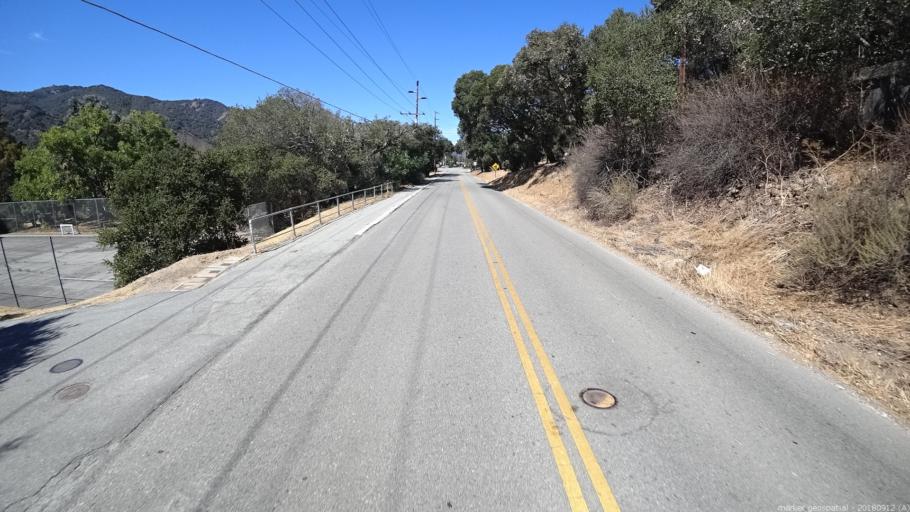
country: US
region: California
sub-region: Monterey County
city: Carmel Valley Village
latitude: 36.4770
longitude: -121.7264
